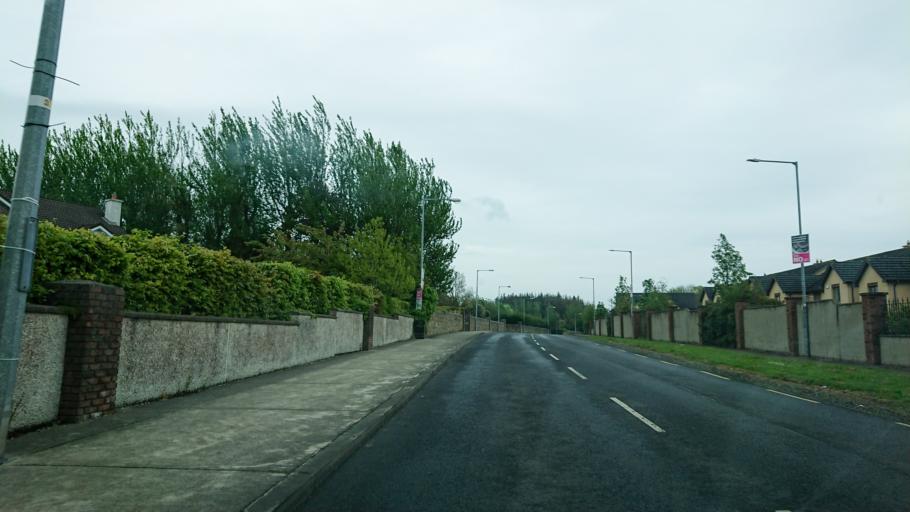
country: IE
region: Munster
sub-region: Waterford
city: Waterford
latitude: 52.2345
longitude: -7.0751
